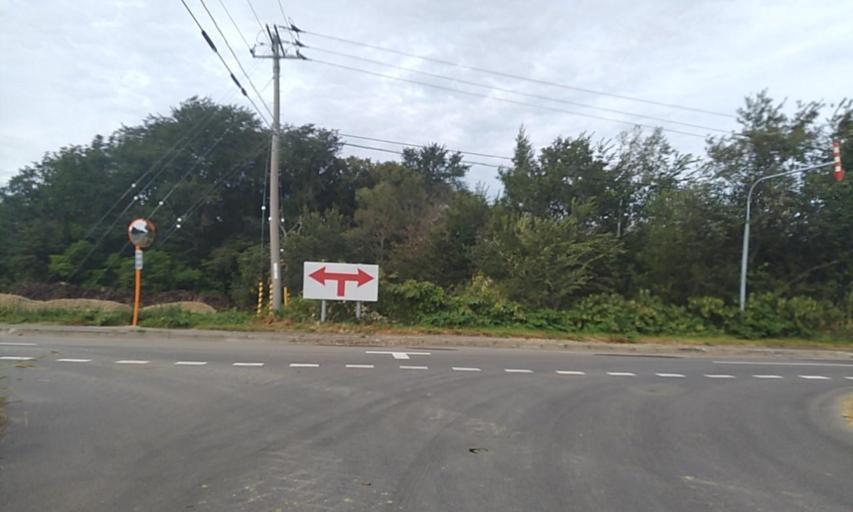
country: JP
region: Hokkaido
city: Abashiri
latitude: 43.7954
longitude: 144.5518
